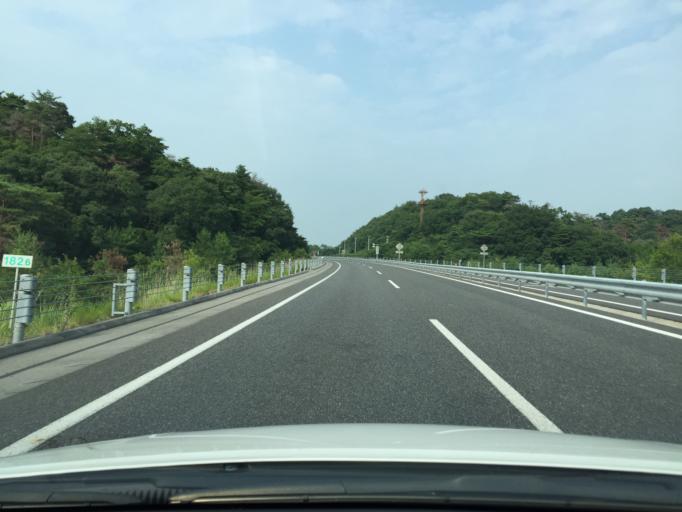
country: JP
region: Fukushima
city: Iwaki
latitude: 37.1087
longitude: 140.8887
